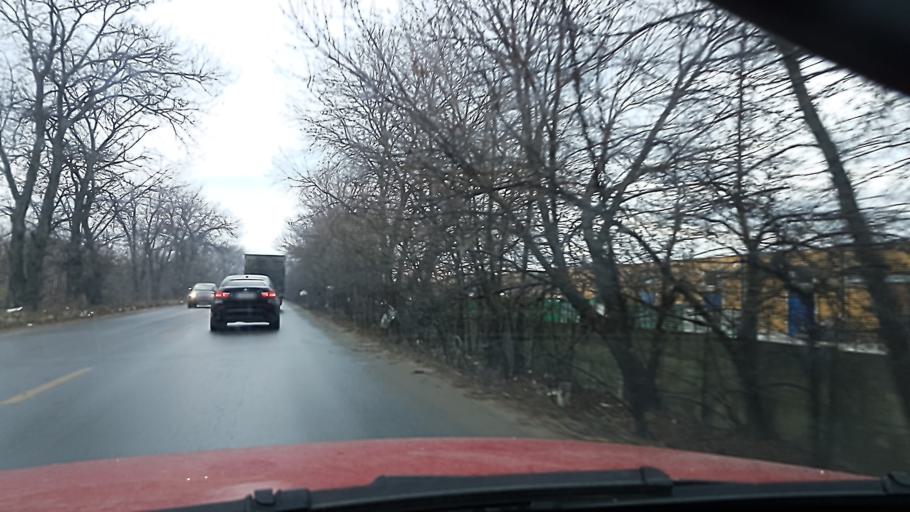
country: RO
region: Ilfov
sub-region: Comuna Glina
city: Catelu
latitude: 44.3925
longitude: 26.2243
